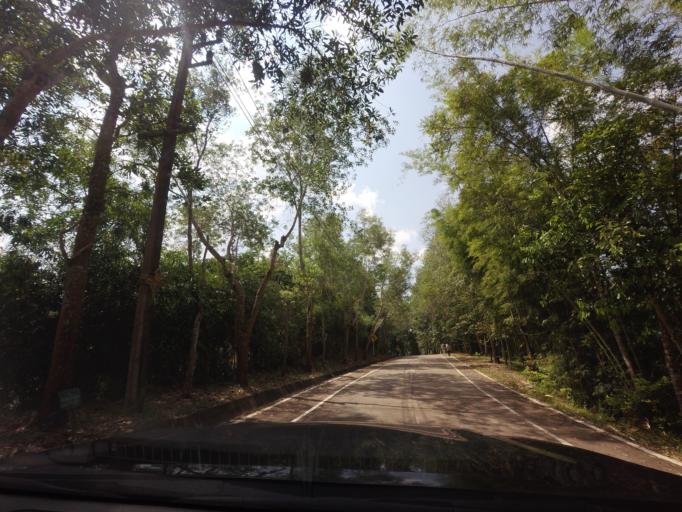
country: TH
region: Nan
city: Bo Kluea
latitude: 19.0178
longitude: 101.2059
